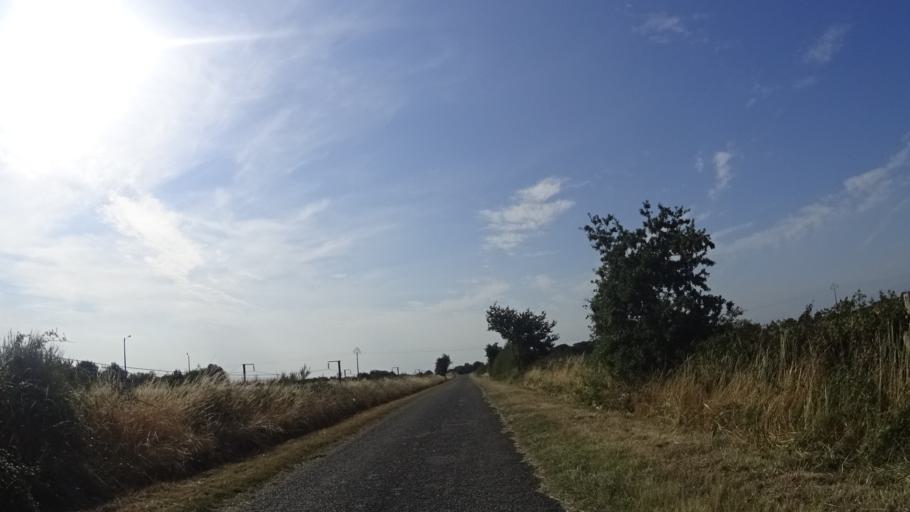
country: FR
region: Pays de la Loire
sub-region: Departement de la Loire-Atlantique
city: Donges
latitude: 47.3198
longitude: -2.0970
